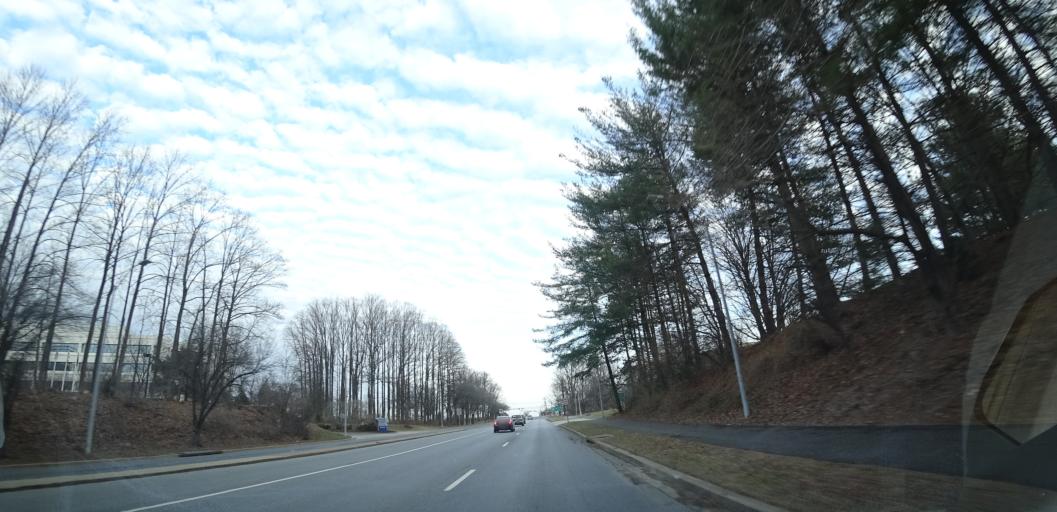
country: US
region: Maryland
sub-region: Montgomery County
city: Derwood
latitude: 39.1067
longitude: -77.1622
